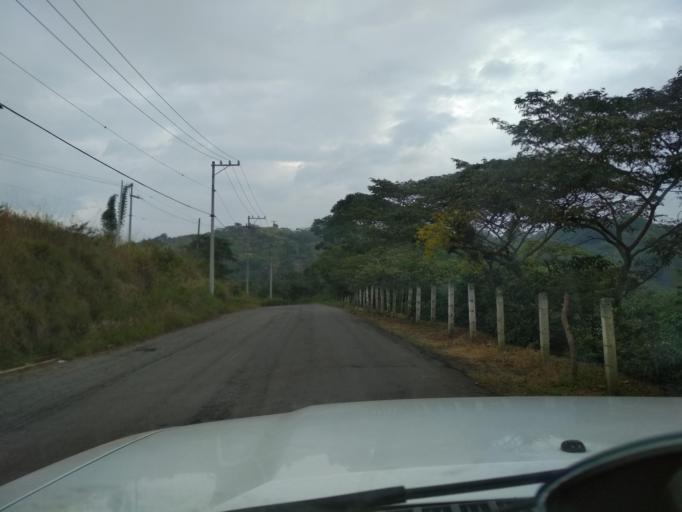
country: MX
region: Veracruz
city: El Castillo
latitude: 19.5657
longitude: -96.8687
